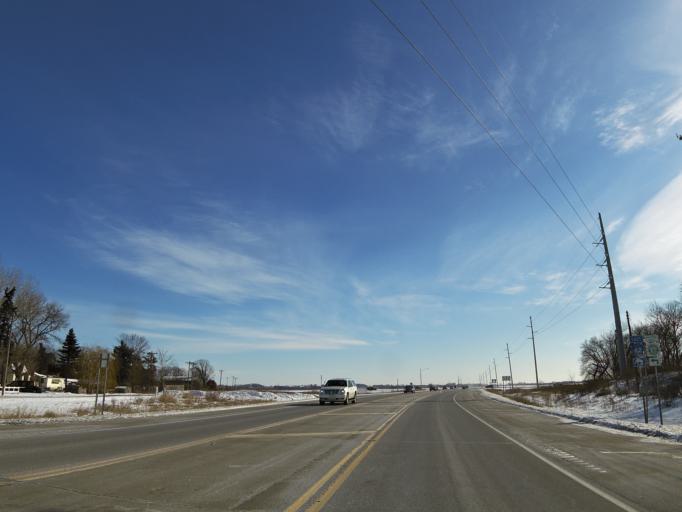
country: US
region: Minnesota
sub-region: Washington County
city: Cottage Grove
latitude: 44.7417
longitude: -92.9539
